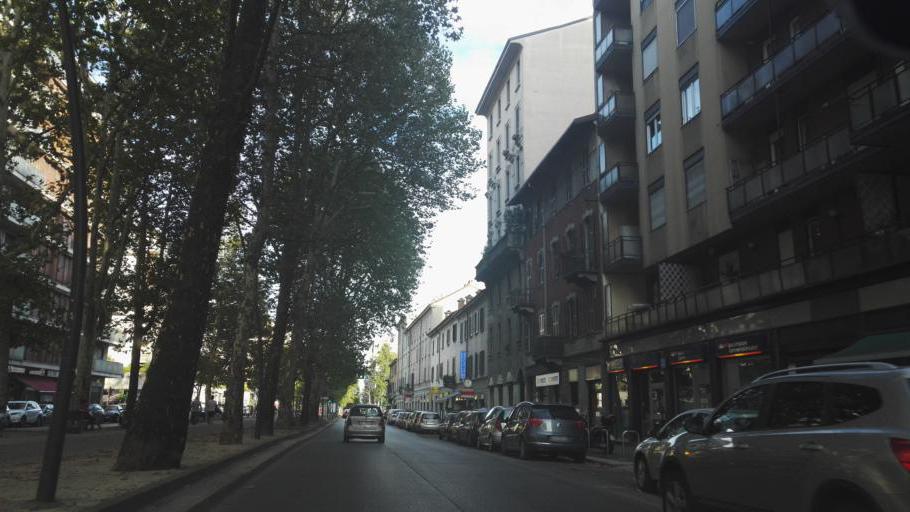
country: IT
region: Lombardy
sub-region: Citta metropolitana di Milano
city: Milano
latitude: 45.4436
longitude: 9.2167
